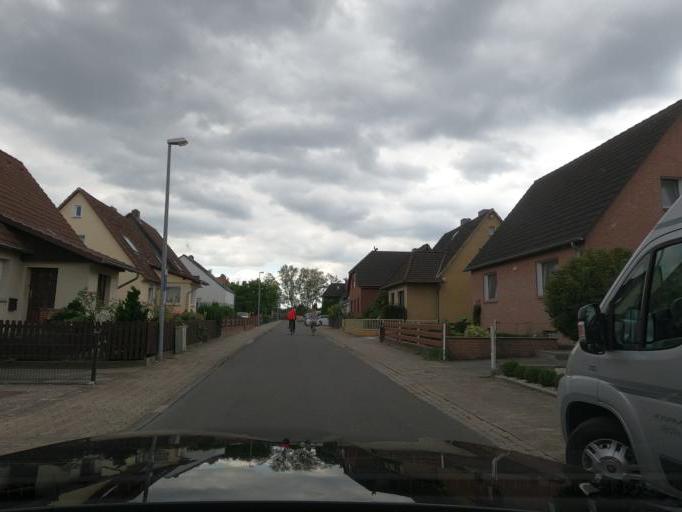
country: DE
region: Lower Saxony
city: Lehrte
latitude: 52.3750
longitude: 9.9100
